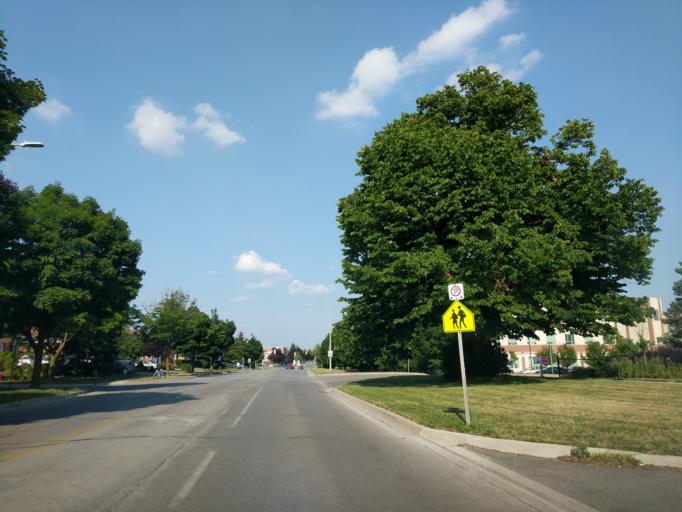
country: CA
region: Ontario
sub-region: York
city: Richmond Hill
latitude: 43.8682
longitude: -79.4162
